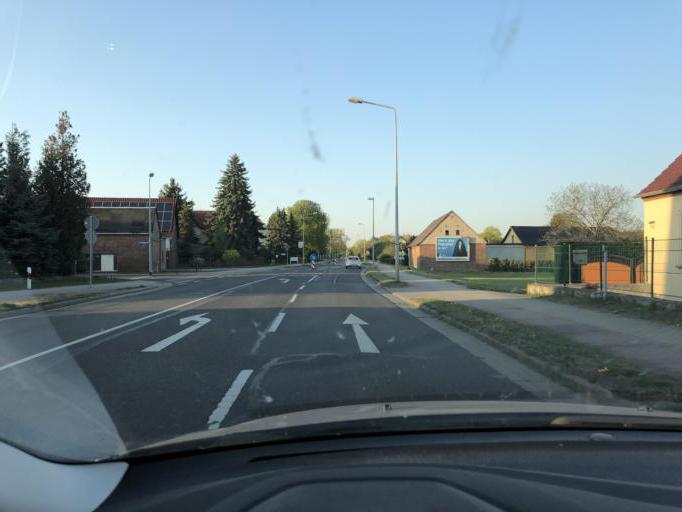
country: DE
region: Brandenburg
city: Spremberg
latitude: 51.5328
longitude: 14.3399
